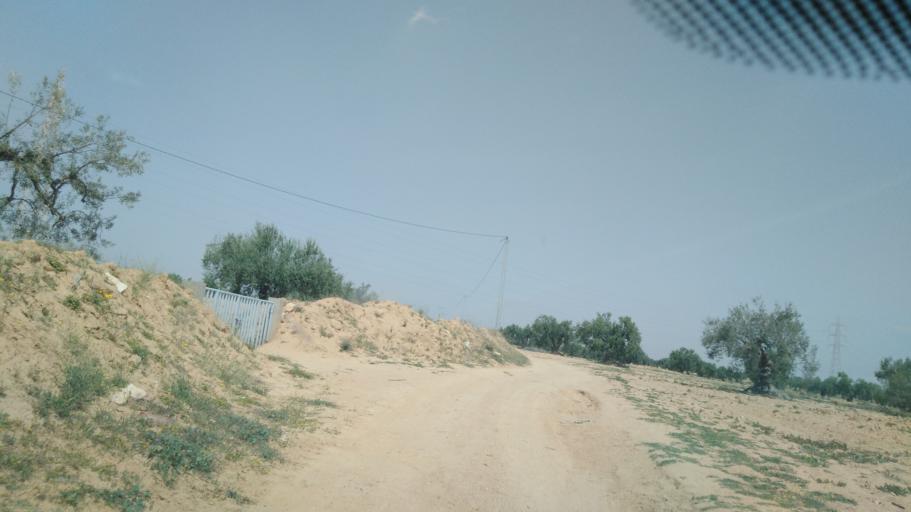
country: TN
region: Safaqis
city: Sfax
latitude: 34.7401
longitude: 10.5718
